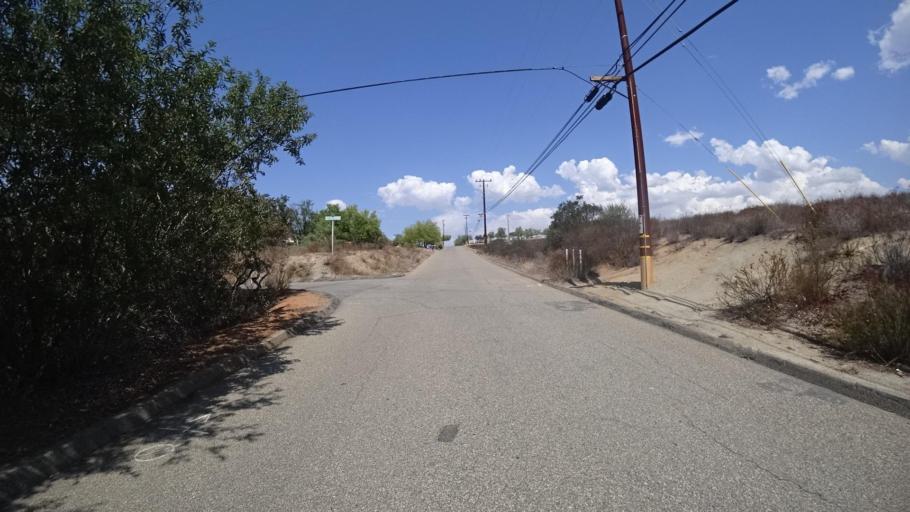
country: US
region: California
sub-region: San Diego County
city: Valley Center
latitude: 33.2545
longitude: -116.9883
